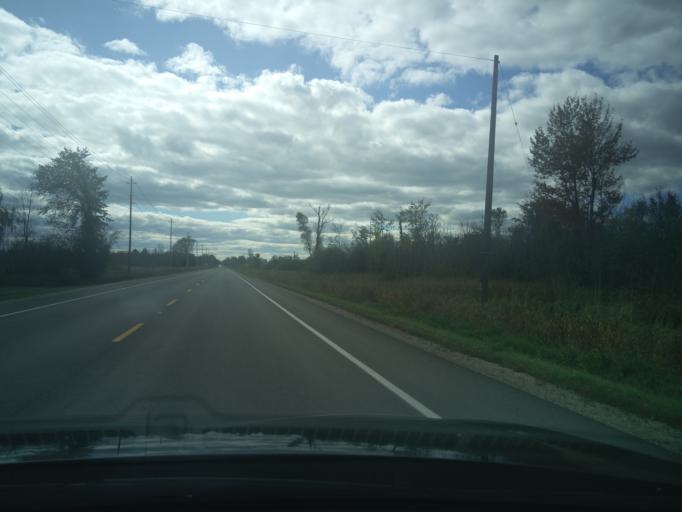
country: CA
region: Ontario
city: Perth
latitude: 44.9135
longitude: -76.2330
